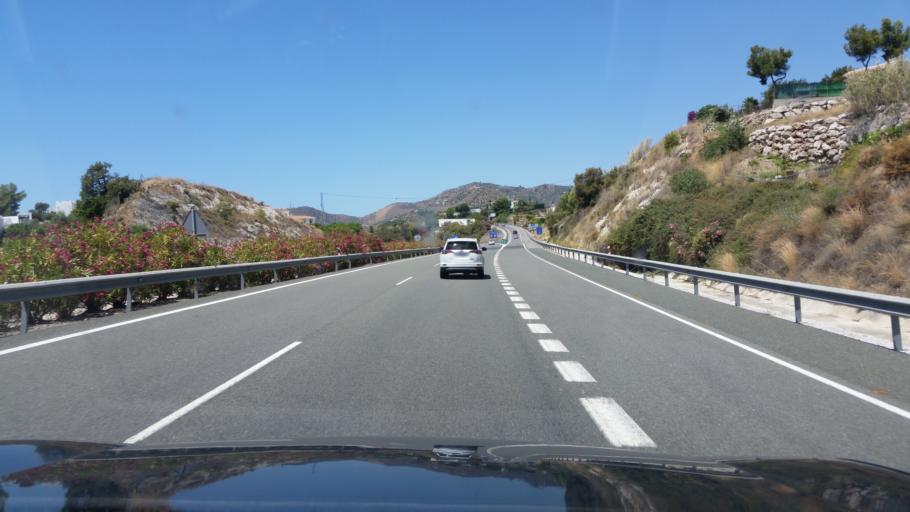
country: ES
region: Andalusia
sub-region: Provincia de Malaga
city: Nerja
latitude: 36.7641
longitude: -3.8823
